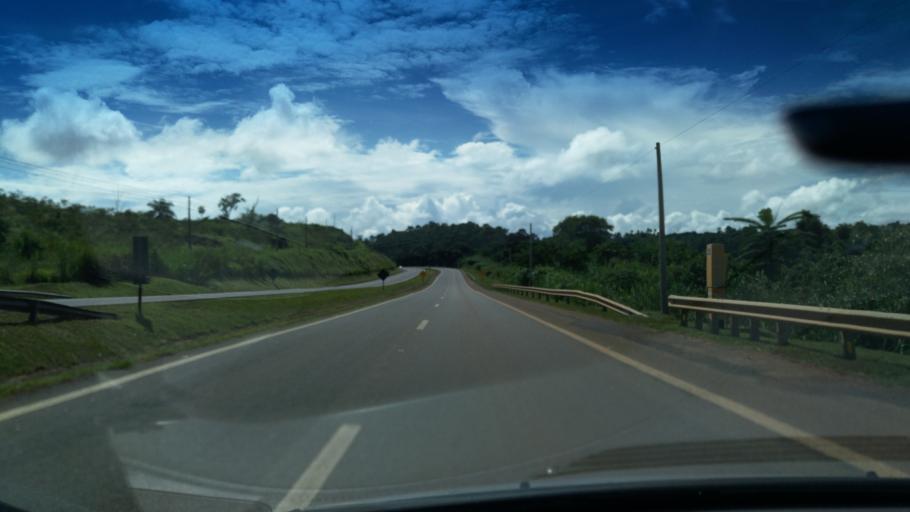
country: BR
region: Sao Paulo
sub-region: Santo Antonio Do Jardim
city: Espirito Santo do Pinhal
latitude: -22.2216
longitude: -46.7907
